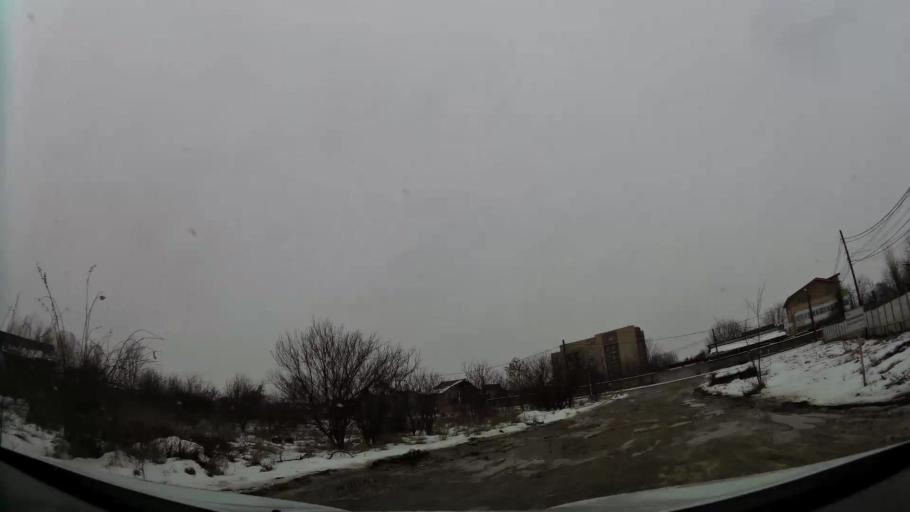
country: RO
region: Ilfov
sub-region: Comuna Chiajna
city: Rosu
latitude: 44.4056
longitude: 26.0121
